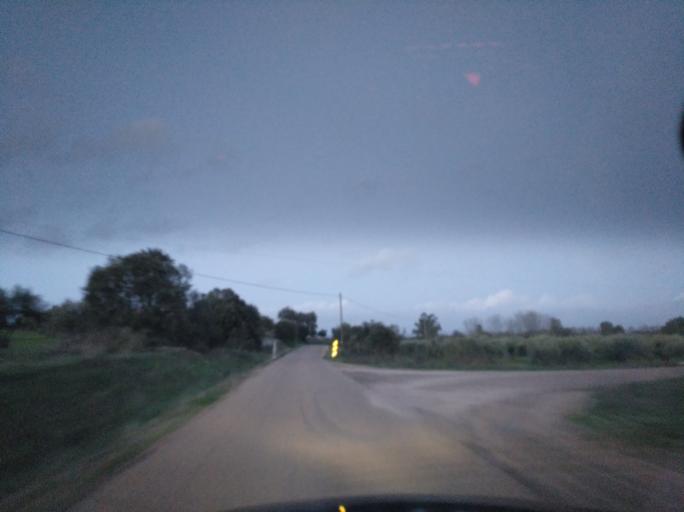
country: PT
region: Portalegre
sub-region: Campo Maior
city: Campo Maior
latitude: 39.0775
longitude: -7.0213
